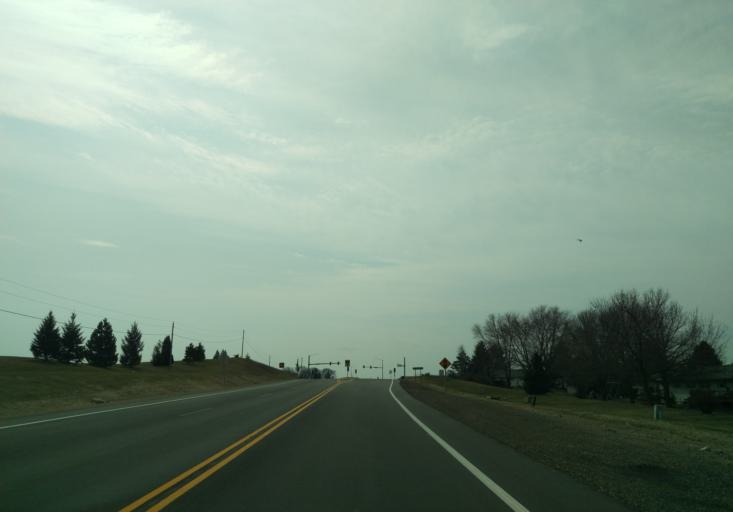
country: US
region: Wisconsin
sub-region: Dane County
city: Waunakee
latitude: 43.1798
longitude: -89.4618
